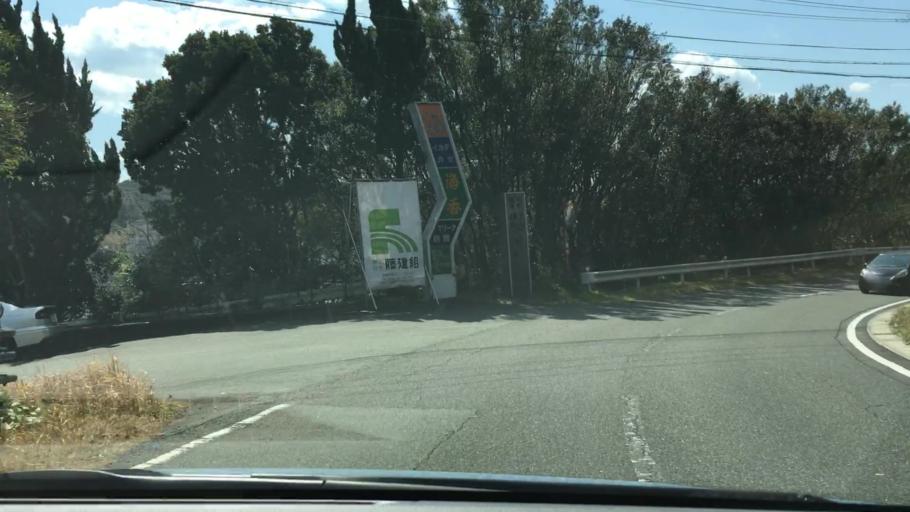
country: JP
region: Mie
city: Toba
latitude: 34.4463
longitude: 136.8836
